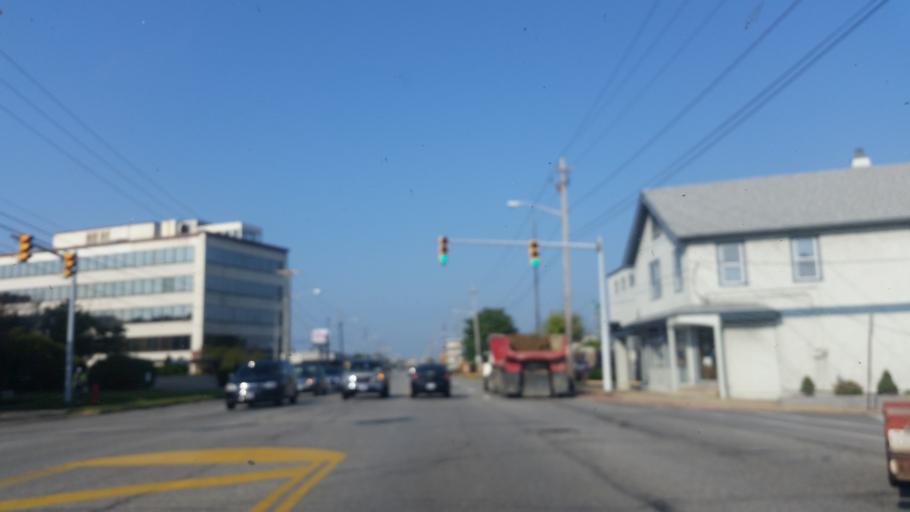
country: US
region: Ohio
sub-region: Cuyahoga County
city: Rocky River
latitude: 41.4636
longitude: -81.8472
